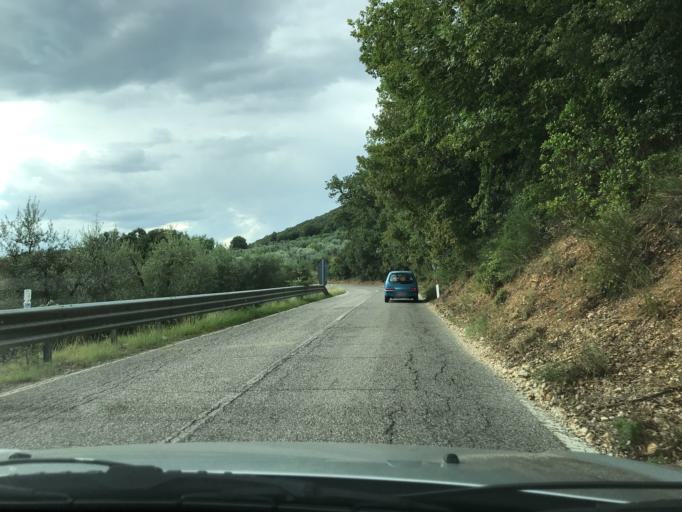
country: IT
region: Umbria
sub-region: Provincia di Terni
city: Guardea
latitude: 42.6383
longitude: 12.2918
